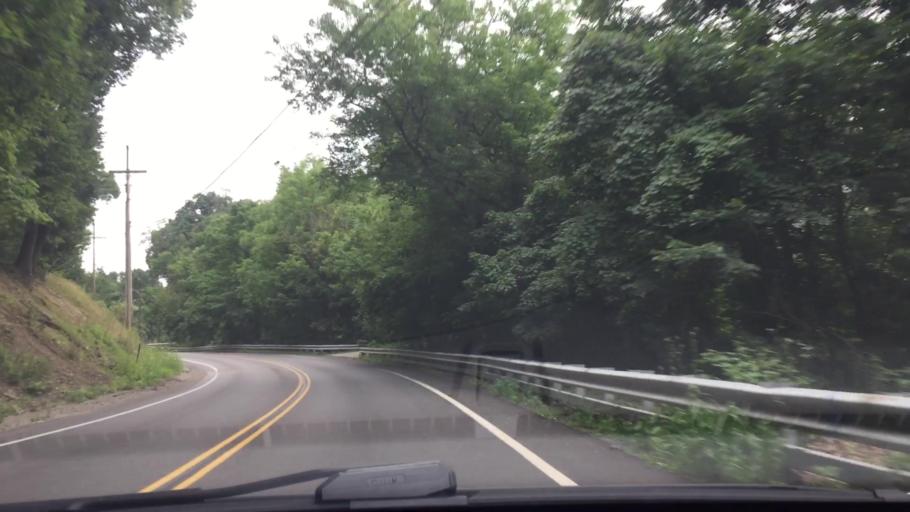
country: US
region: Pennsylvania
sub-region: Allegheny County
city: Rennerdale
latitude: 40.3913
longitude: -80.1592
